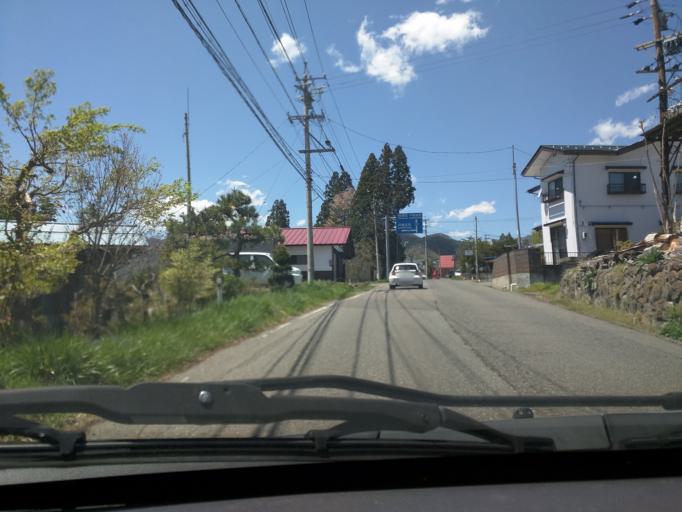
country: JP
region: Nagano
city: Nagano-shi
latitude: 36.7057
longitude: 138.0930
